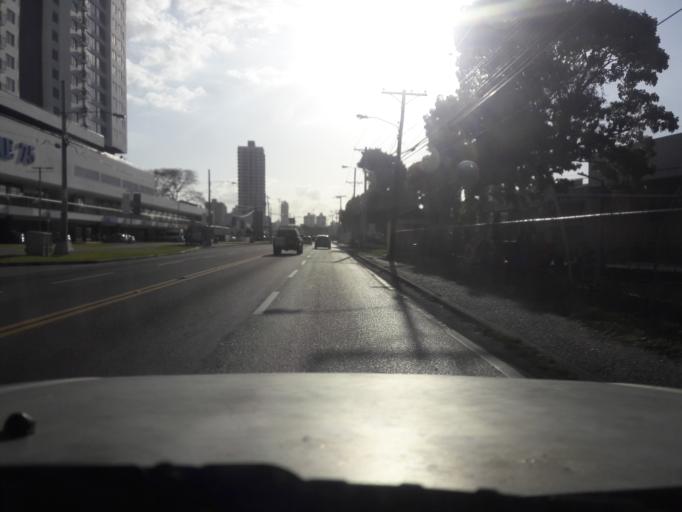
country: PA
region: Panama
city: Panama
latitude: 9.0167
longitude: -79.4958
